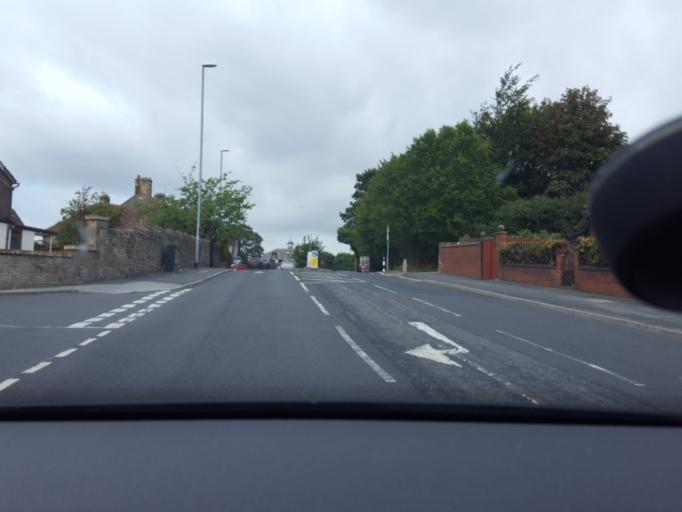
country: GB
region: England
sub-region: City and Borough of Leeds
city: Gildersome
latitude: 53.7988
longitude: -1.6076
